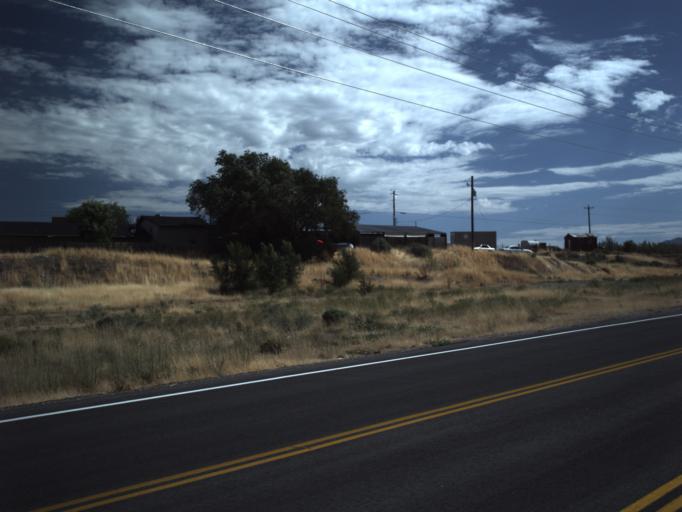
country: US
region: Utah
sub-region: Utah County
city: Genola
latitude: 39.9855
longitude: -111.8190
